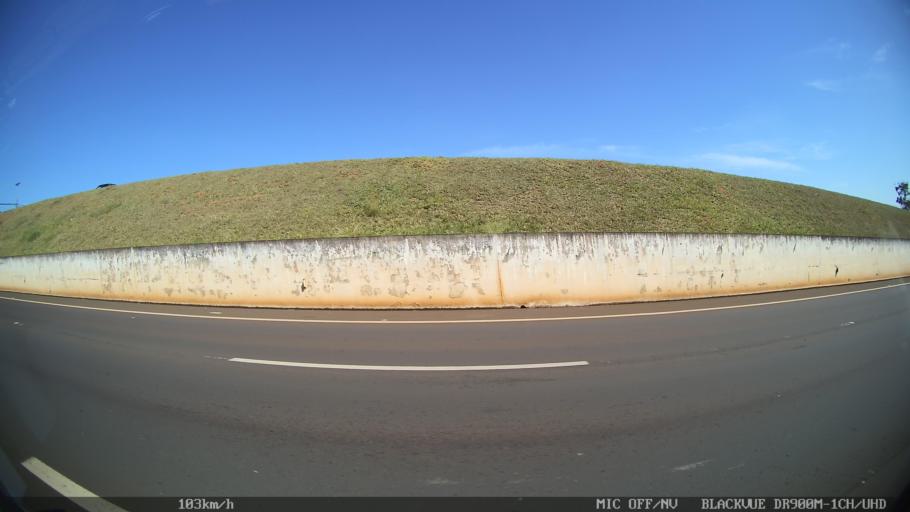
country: BR
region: Sao Paulo
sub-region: Franca
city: Franca
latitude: -20.5404
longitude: -47.4210
